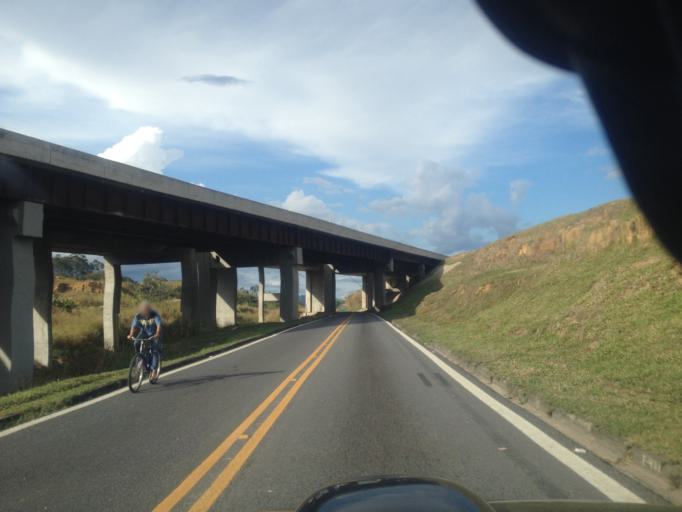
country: BR
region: Rio de Janeiro
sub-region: Porto Real
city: Porto Real
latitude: -22.4501
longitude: -44.3275
